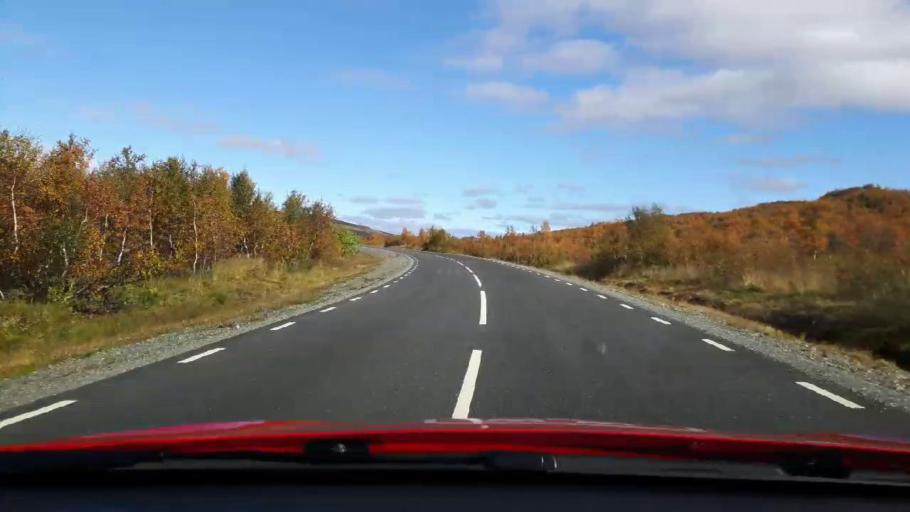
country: NO
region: Nordland
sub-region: Hattfjelldal
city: Hattfjelldal
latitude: 64.9962
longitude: 14.2375
